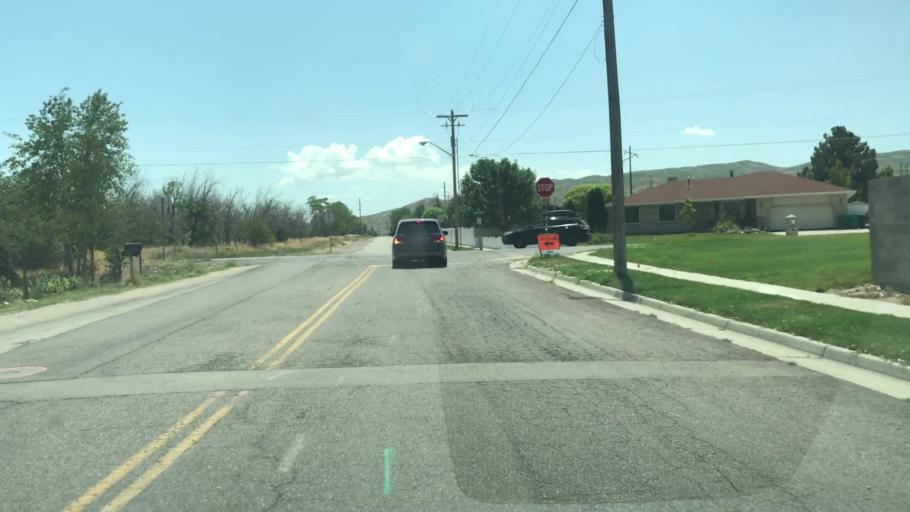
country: US
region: Utah
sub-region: Salt Lake County
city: Bluffdale
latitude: 40.4791
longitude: -111.9484
